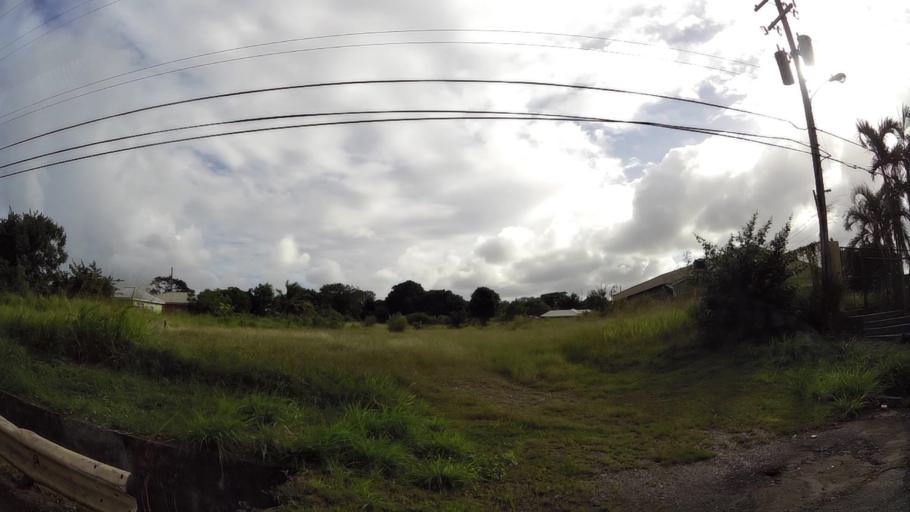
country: AG
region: Saint John
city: Saint John's
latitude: 17.1243
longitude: -61.8274
